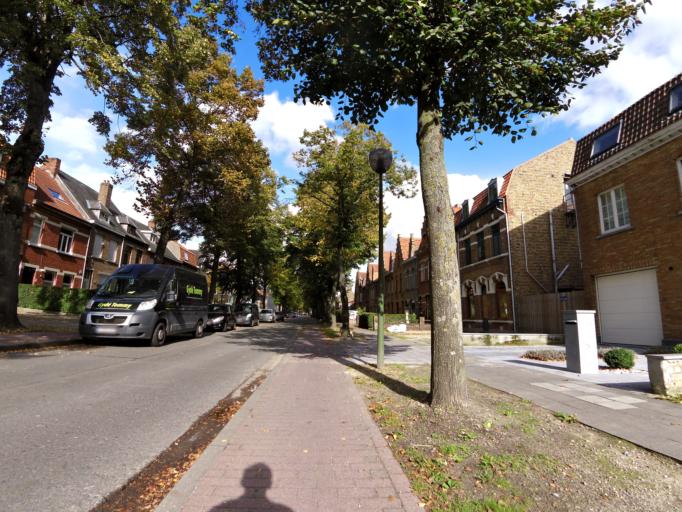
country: BE
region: Flanders
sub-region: Provincie West-Vlaanderen
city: Sint-Kruis
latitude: 51.2240
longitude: 3.2348
